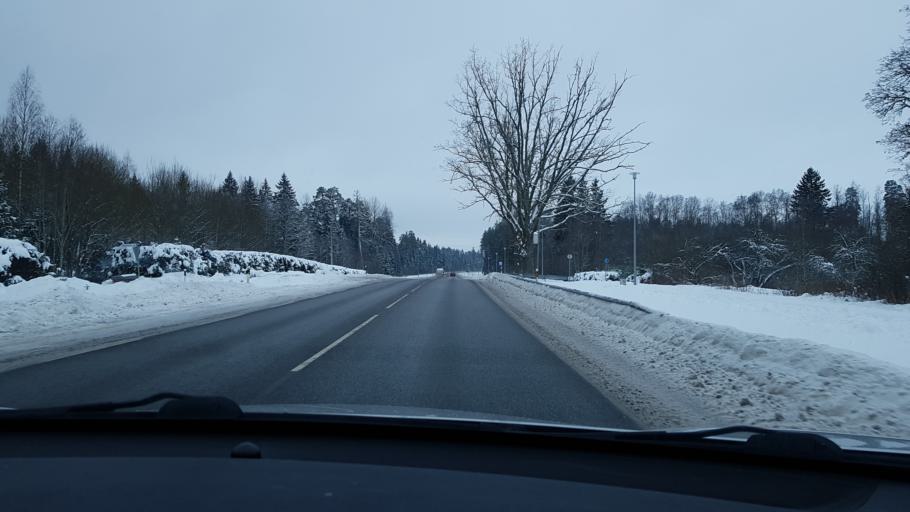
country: EE
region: Jaervamaa
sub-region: Paide linn
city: Paide
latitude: 58.8673
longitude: 25.4937
